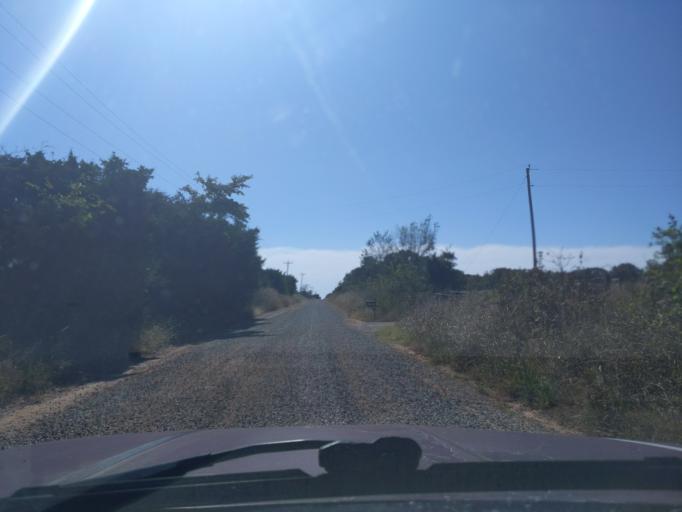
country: US
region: Oklahoma
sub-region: Creek County
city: Bristow
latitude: 35.6599
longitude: -96.4234
